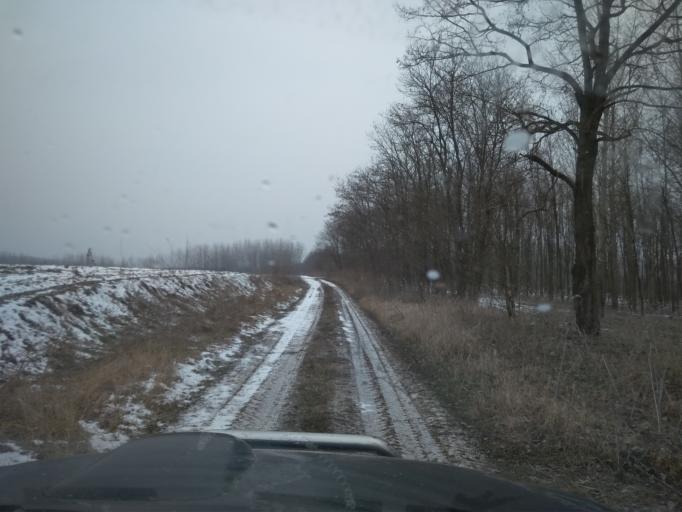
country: HU
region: Szabolcs-Szatmar-Bereg
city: Apagy
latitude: 47.9768
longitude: 21.9148
